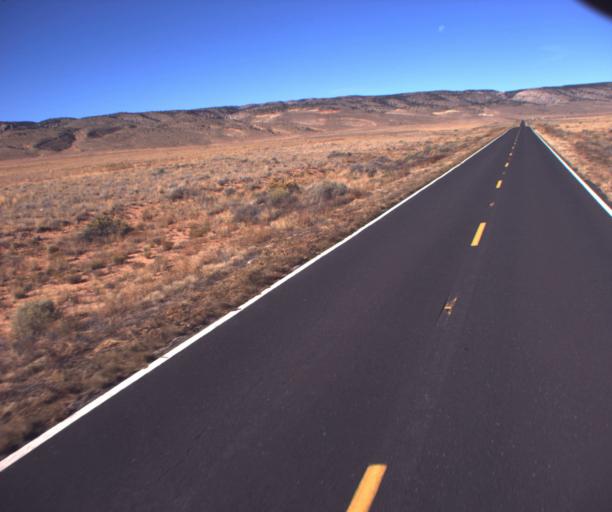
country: US
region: Arizona
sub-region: Coconino County
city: Fredonia
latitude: 36.7246
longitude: -112.0245
